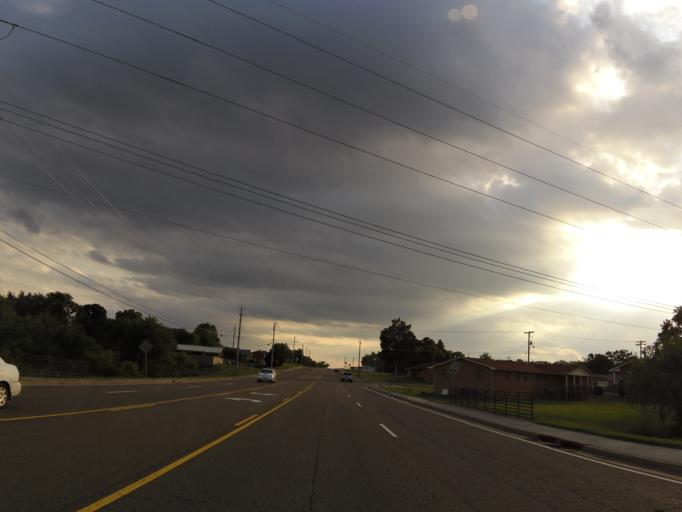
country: US
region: Tennessee
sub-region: Knox County
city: Knoxville
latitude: 36.0824
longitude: -83.9363
